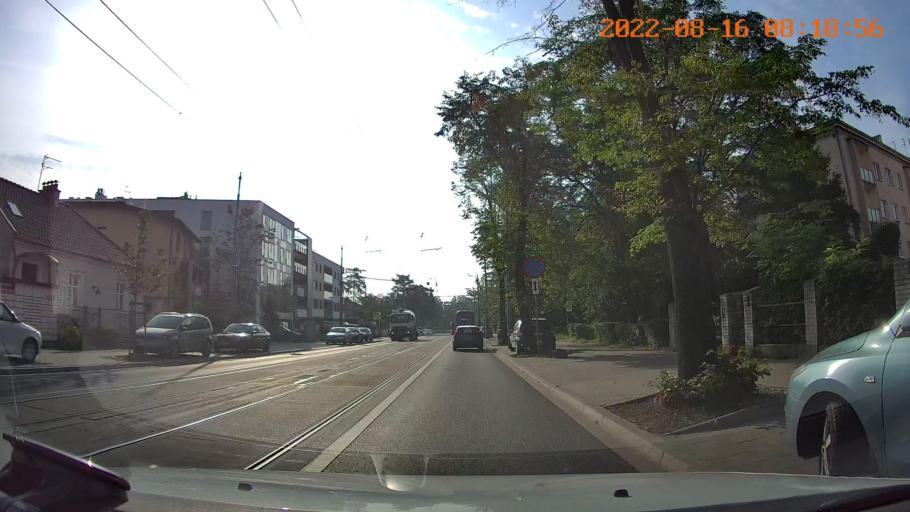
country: PL
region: Lesser Poland Voivodeship
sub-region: Krakow
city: Krakow
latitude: 50.0766
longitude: 19.9038
